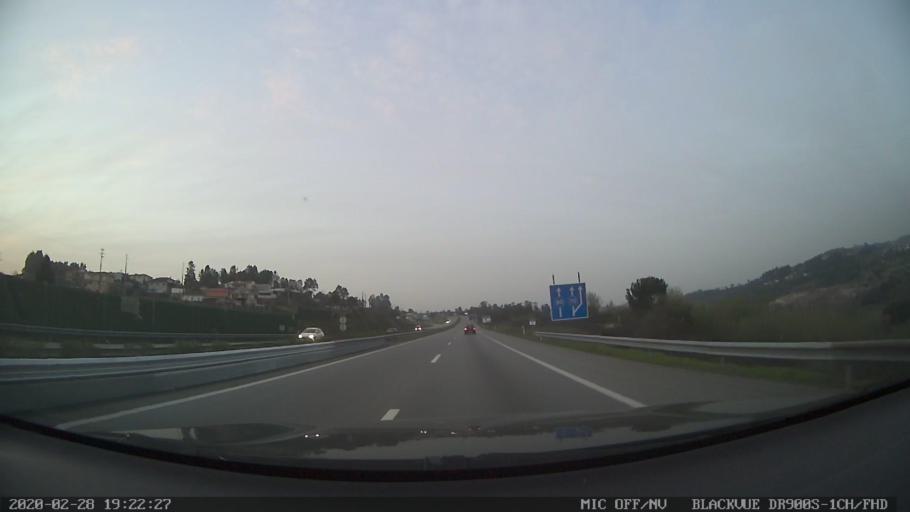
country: PT
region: Porto
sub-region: Marco de Canaveses
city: Marco de Canavezes
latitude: 41.2297
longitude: -8.1726
